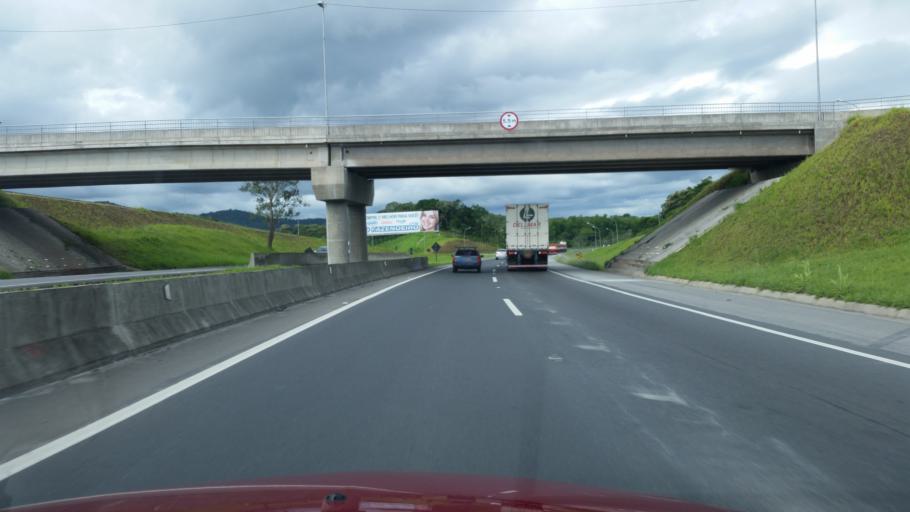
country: BR
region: Sao Paulo
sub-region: Miracatu
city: Miracatu
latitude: -24.2957
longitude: -47.4803
